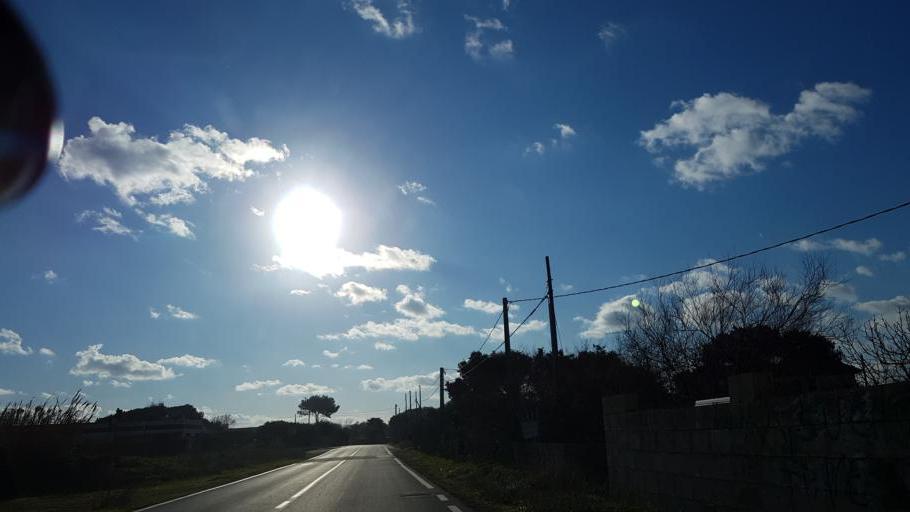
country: IT
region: Apulia
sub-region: Provincia di Brindisi
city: Materdomini
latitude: 40.6683
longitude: 17.9478
